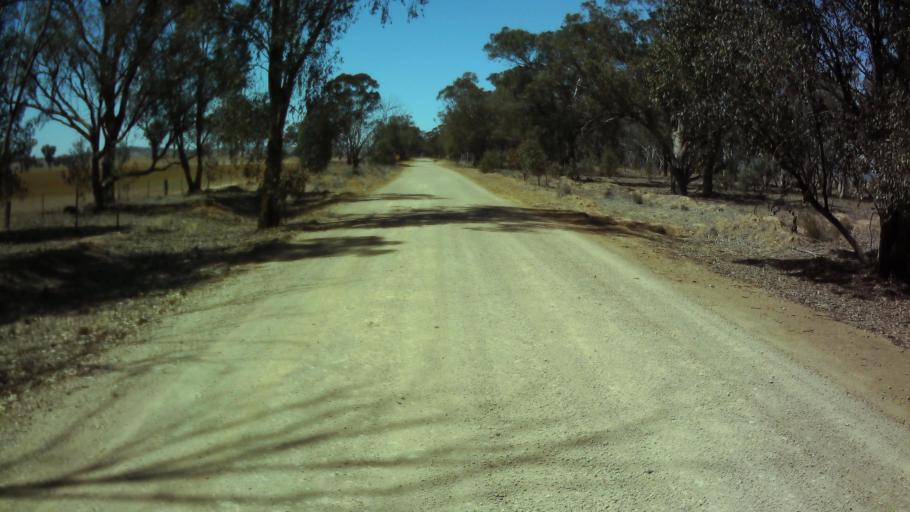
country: AU
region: New South Wales
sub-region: Weddin
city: Grenfell
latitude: -33.8714
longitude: 148.0886
